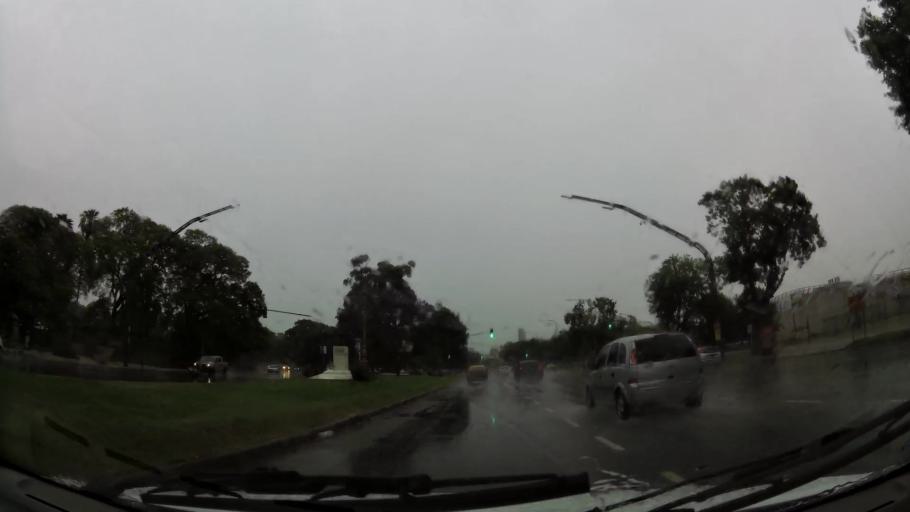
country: AR
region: Buenos Aires F.D.
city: Retiro
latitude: -34.5851
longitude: -58.3888
